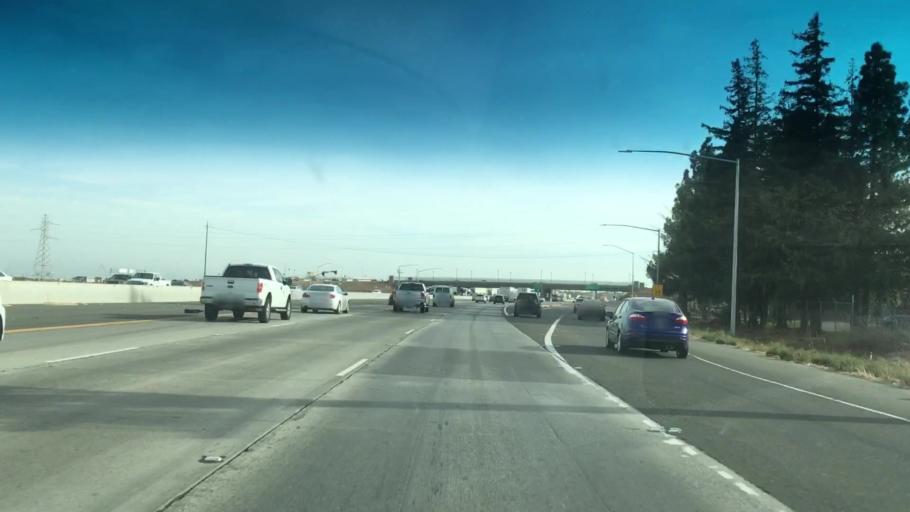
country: US
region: California
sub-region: Sacramento County
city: Parkway
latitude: 38.4705
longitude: -121.4994
